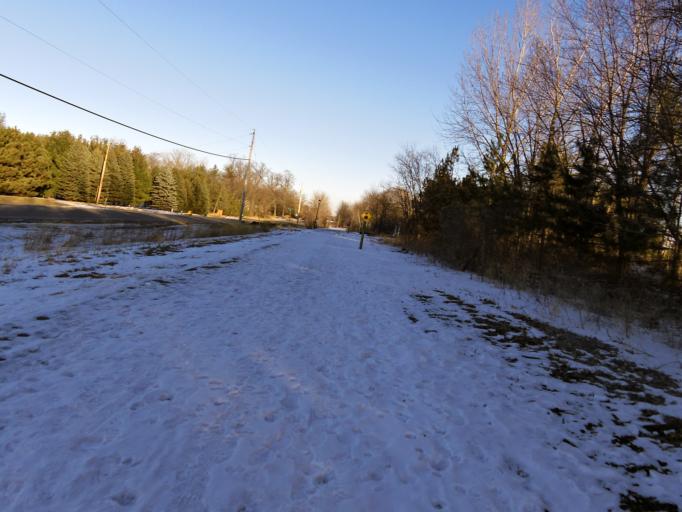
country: US
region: Minnesota
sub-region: Washington County
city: Grant
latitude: 45.0721
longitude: -92.8581
